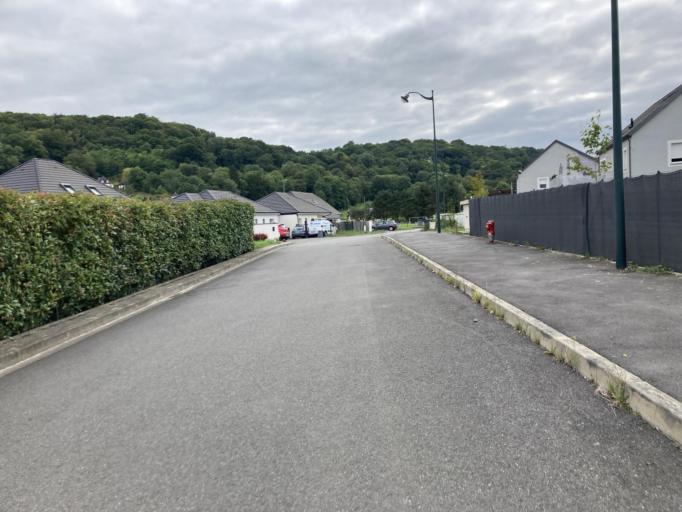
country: FR
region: Aquitaine
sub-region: Departement des Pyrenees-Atlantiques
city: Arbus
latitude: 43.3349
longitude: -0.5039
